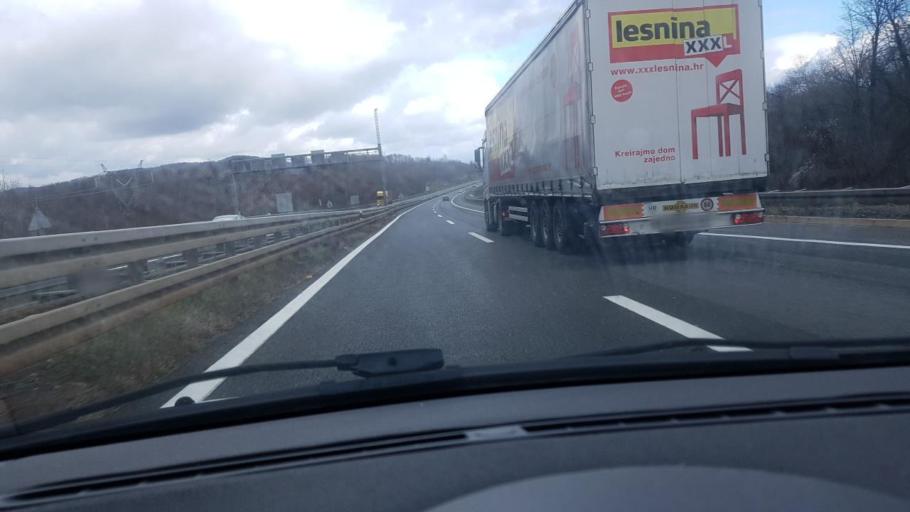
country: HR
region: Karlovacka
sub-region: Grad Ogulin
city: Ogulin
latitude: 45.3996
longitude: 15.2175
